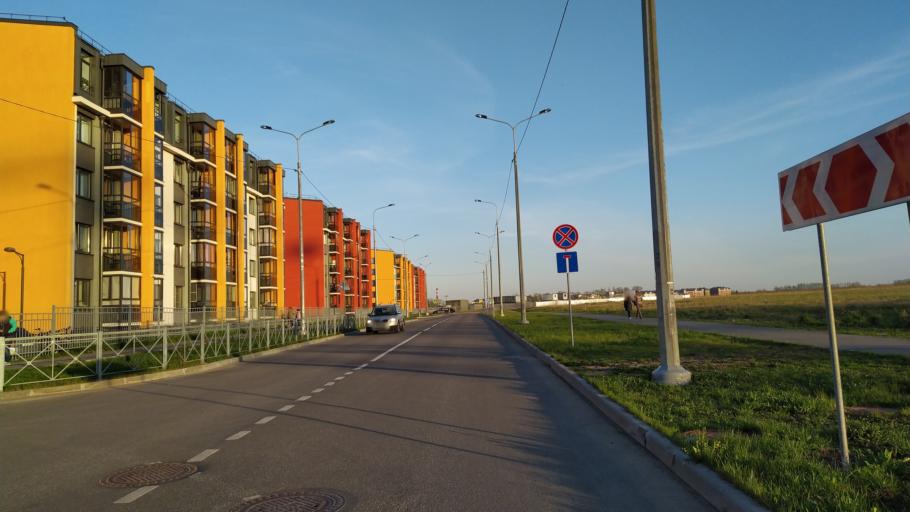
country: RU
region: St.-Petersburg
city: Pushkin
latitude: 59.6985
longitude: 30.4046
